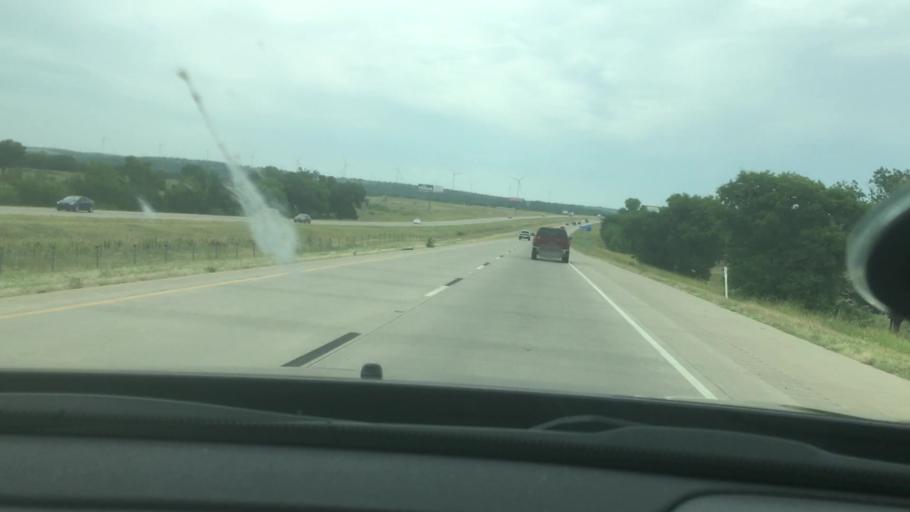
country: US
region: Oklahoma
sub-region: Carter County
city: Ardmore
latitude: 34.3207
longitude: -97.1556
